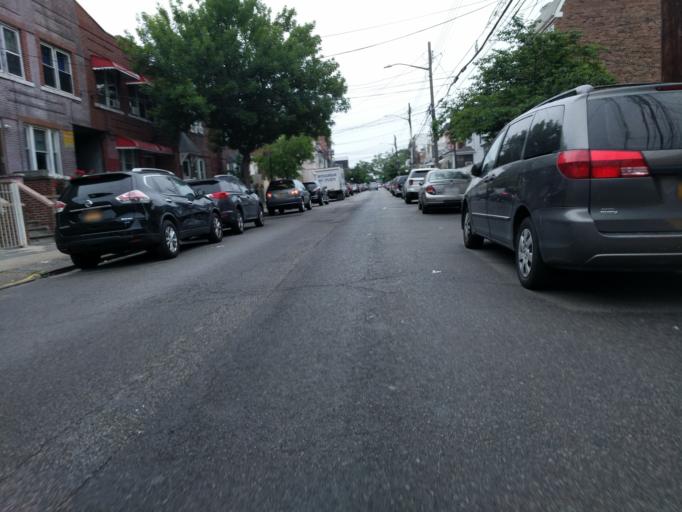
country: US
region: New York
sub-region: Queens County
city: Borough of Queens
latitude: 40.7545
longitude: -73.8578
